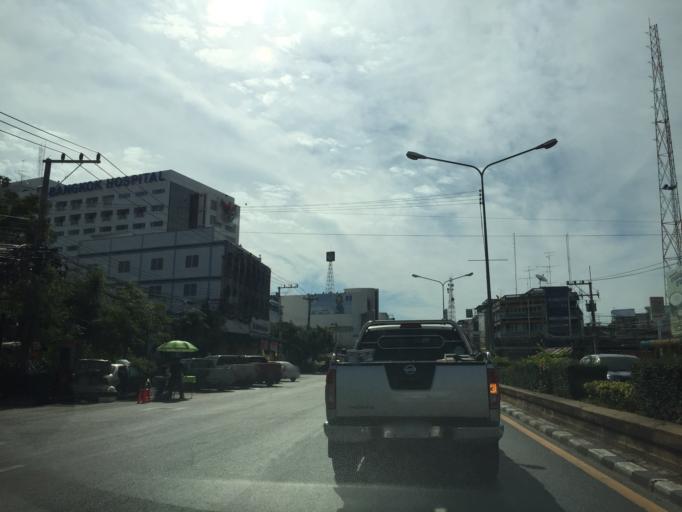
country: TH
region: Phitsanulok
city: Phitsanulok
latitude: 16.8173
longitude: 100.2718
